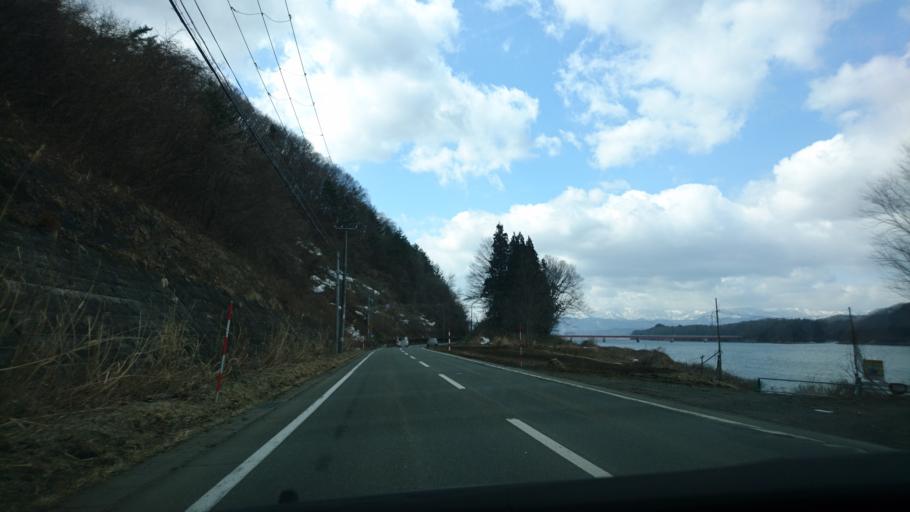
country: JP
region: Iwate
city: Shizukuishi
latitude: 39.6841
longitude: 141.0304
